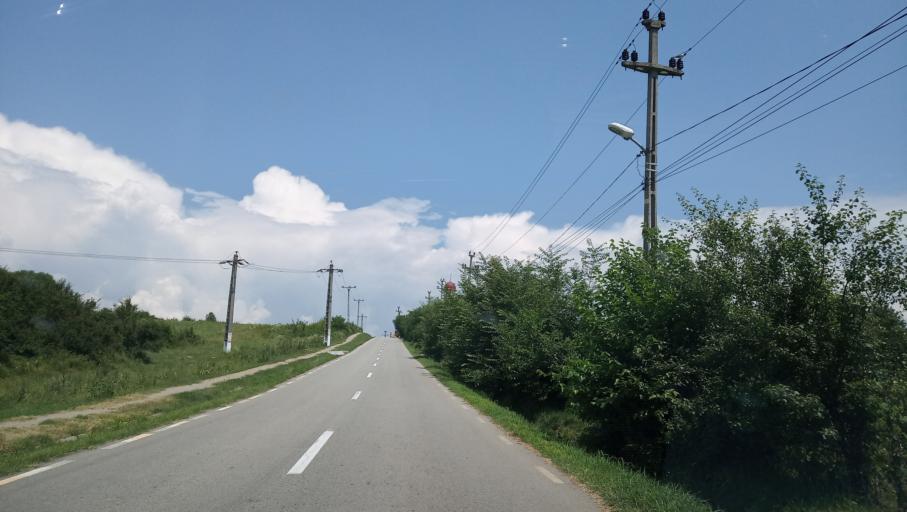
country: RO
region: Gorj
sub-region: Comuna Turcinesti
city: Turcinesti
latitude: 45.0437
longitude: 23.3432
